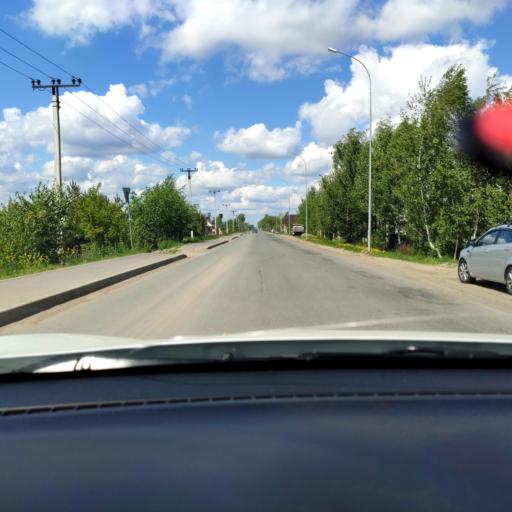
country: RU
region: Tatarstan
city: Stolbishchi
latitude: 55.6965
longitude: 49.1932
